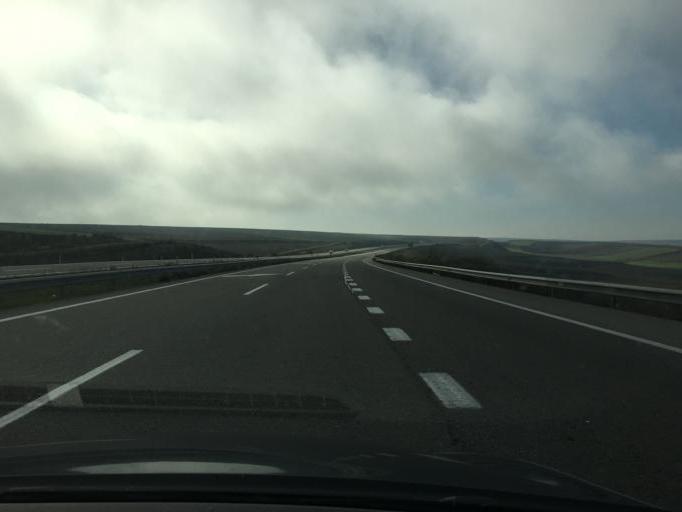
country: ES
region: Castille and Leon
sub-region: Provincia de Burgos
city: Vallarta de Bureba
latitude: 42.6098
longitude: -3.2051
